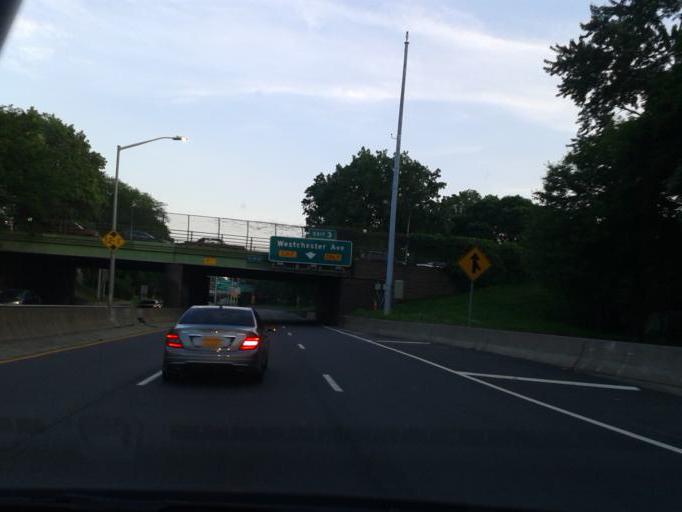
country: US
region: New York
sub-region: Bronx
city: The Bronx
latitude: 40.8349
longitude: -73.8742
